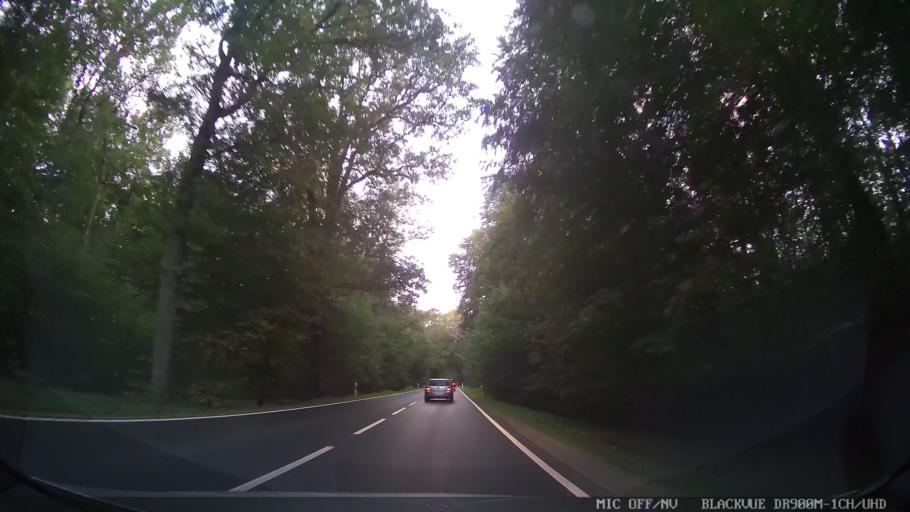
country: DE
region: Schleswig-Holstein
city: Ratekau
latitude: 53.9505
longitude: 10.7221
